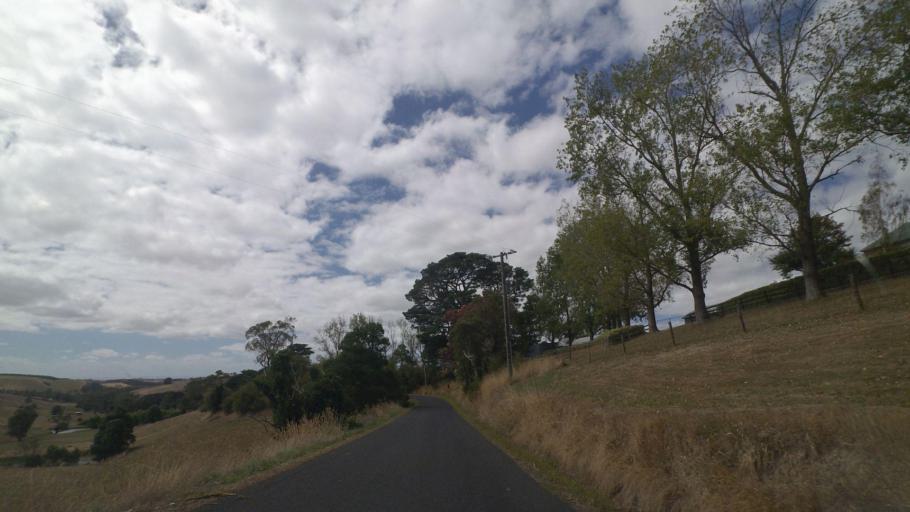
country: AU
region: Victoria
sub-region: Bass Coast
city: North Wonthaggi
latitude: -38.4018
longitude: 145.7670
